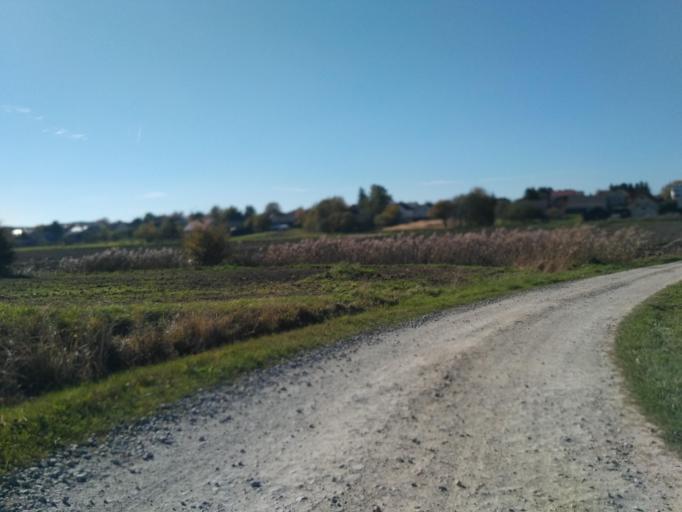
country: PL
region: Subcarpathian Voivodeship
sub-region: Powiat ropczycko-sedziszowski
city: Iwierzyce
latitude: 50.0153
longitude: 21.7569
